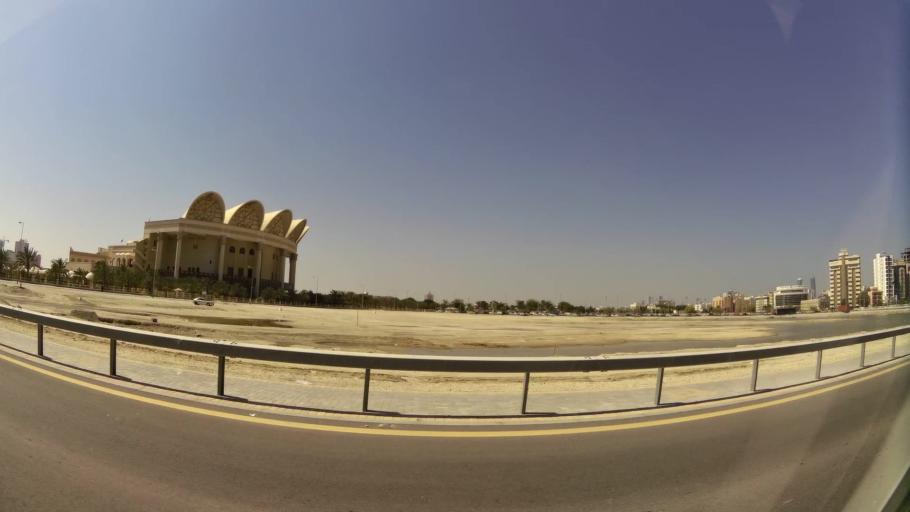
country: BH
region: Manama
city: Manama
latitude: 26.2221
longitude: 50.6010
